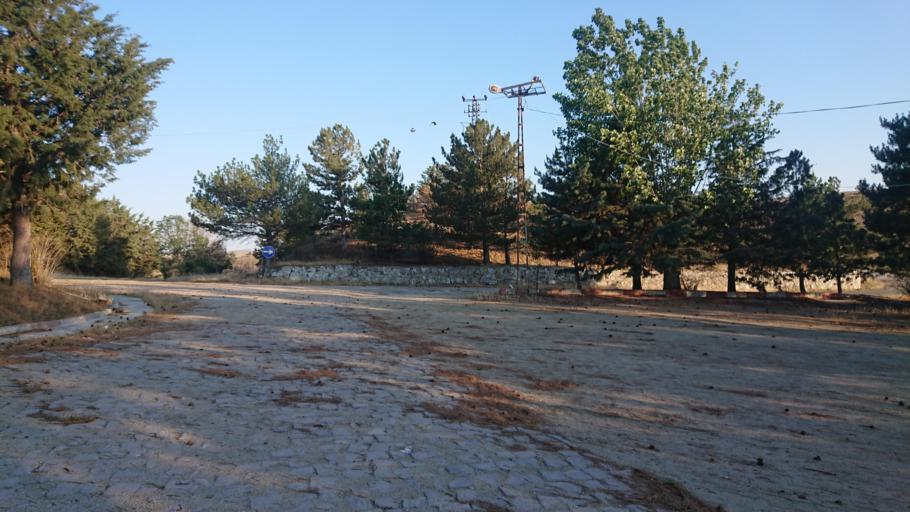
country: TR
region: Aksaray
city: Sariyahsi
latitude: 39.0258
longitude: 33.8923
